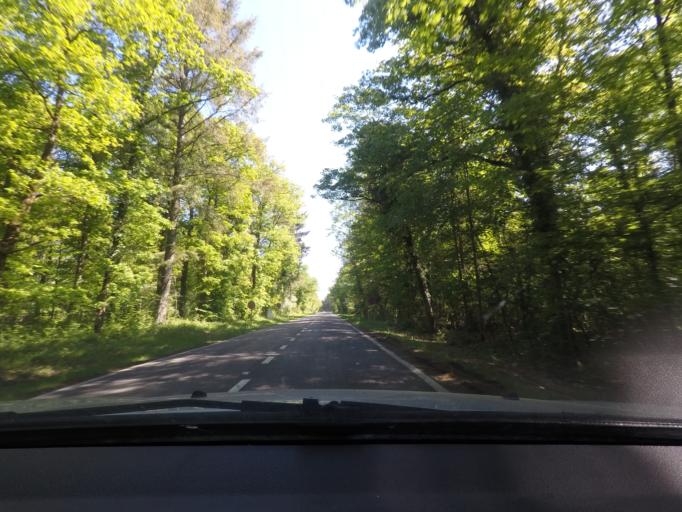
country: BE
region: Wallonia
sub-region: Province du Luxembourg
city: Wellin
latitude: 50.1716
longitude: 5.1137
